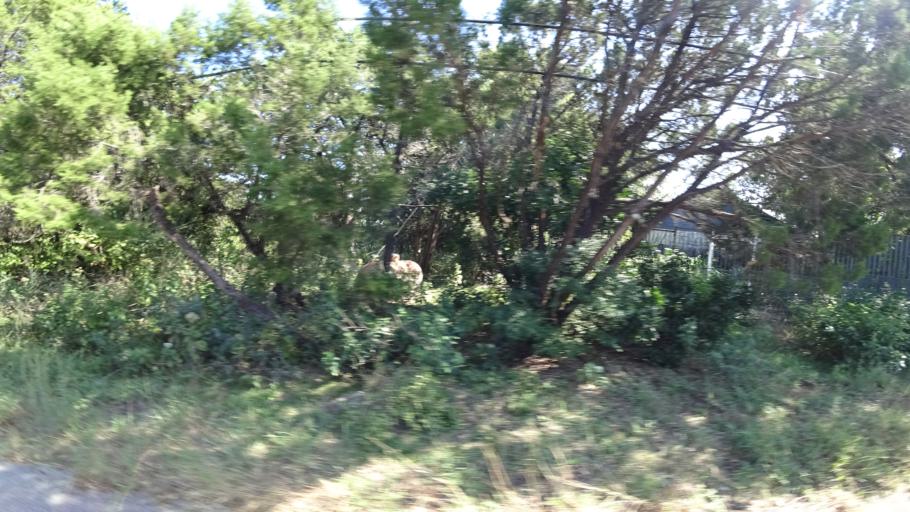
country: US
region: Texas
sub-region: Travis County
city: West Lake Hills
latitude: 30.3015
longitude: -97.8080
